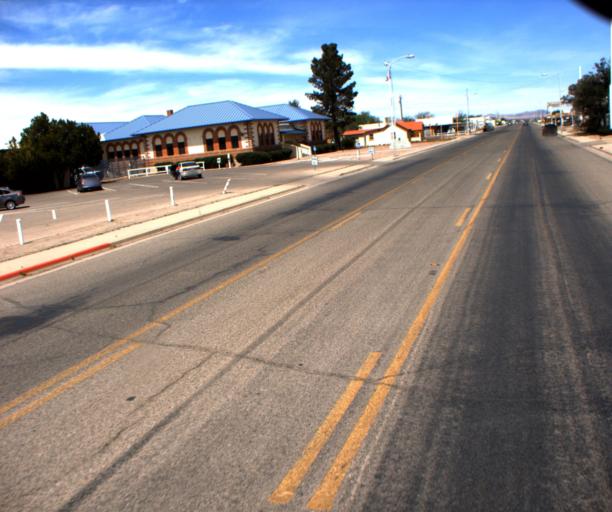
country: US
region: Arizona
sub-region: Cochise County
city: Willcox
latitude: 32.2549
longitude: -109.8309
